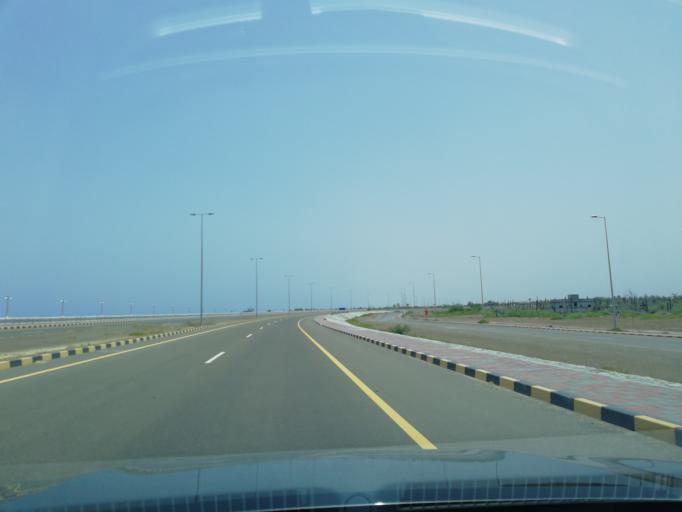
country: OM
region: Al Batinah
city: Shinas
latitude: 24.8446
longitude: 56.4239
